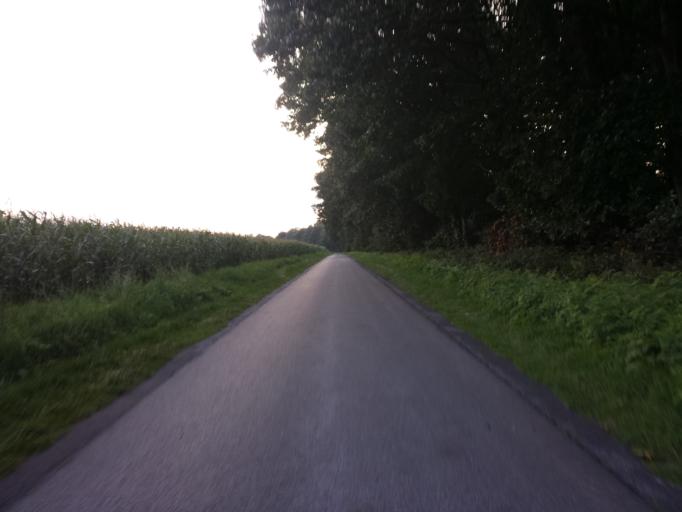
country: DE
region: North Rhine-Westphalia
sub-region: Regierungsbezirk Detmold
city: Harsewinkel
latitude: 51.9747
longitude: 8.2496
